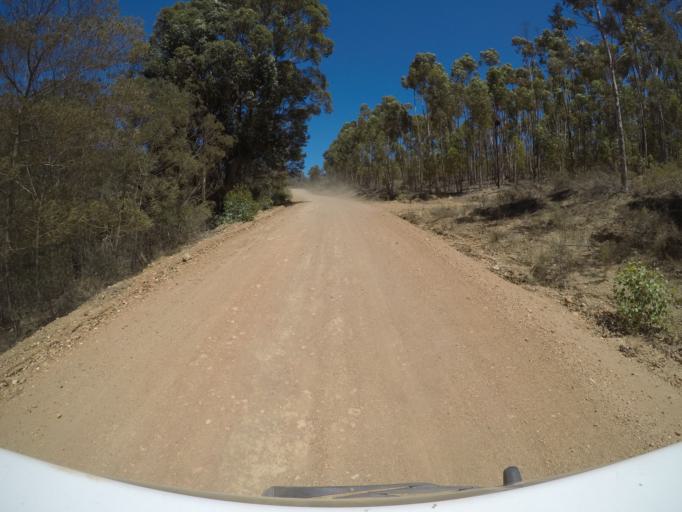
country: ZA
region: Western Cape
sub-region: Overberg District Municipality
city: Caledon
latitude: -34.1575
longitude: 19.2293
